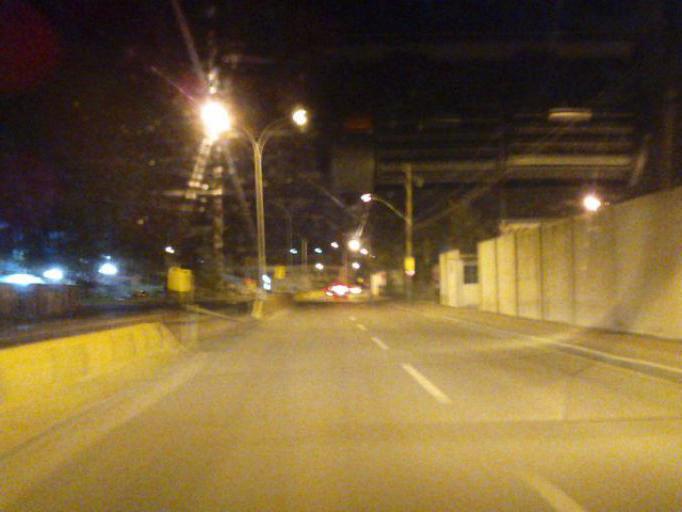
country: BR
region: Santa Catarina
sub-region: Itajai
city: Itajai
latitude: -26.9018
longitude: -48.6661
